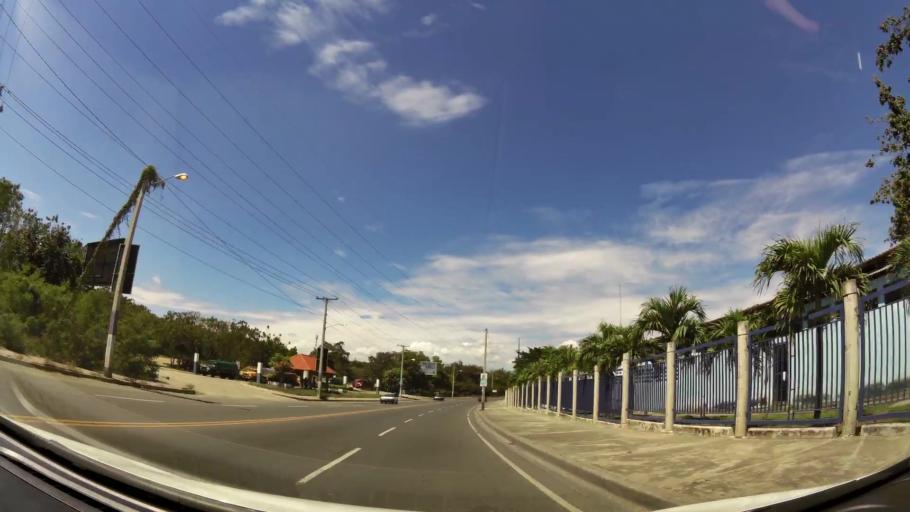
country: DO
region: Santiago
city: Santiago de los Caballeros
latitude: 19.4409
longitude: -70.7028
